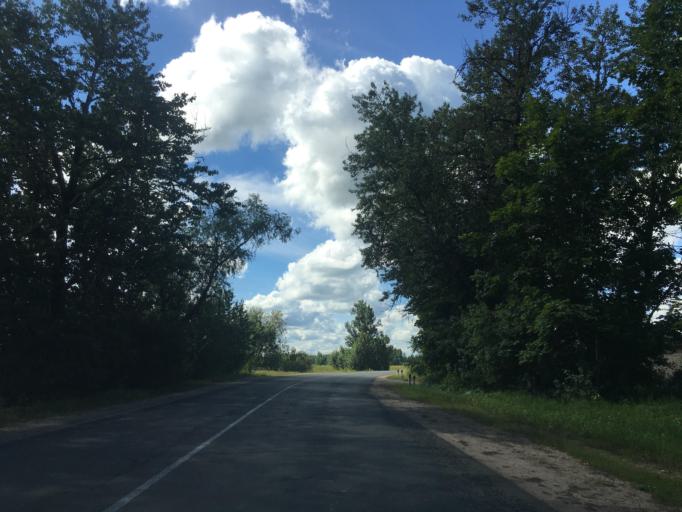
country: RU
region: Pskov
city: Pskov
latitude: 57.7798
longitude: 28.1685
